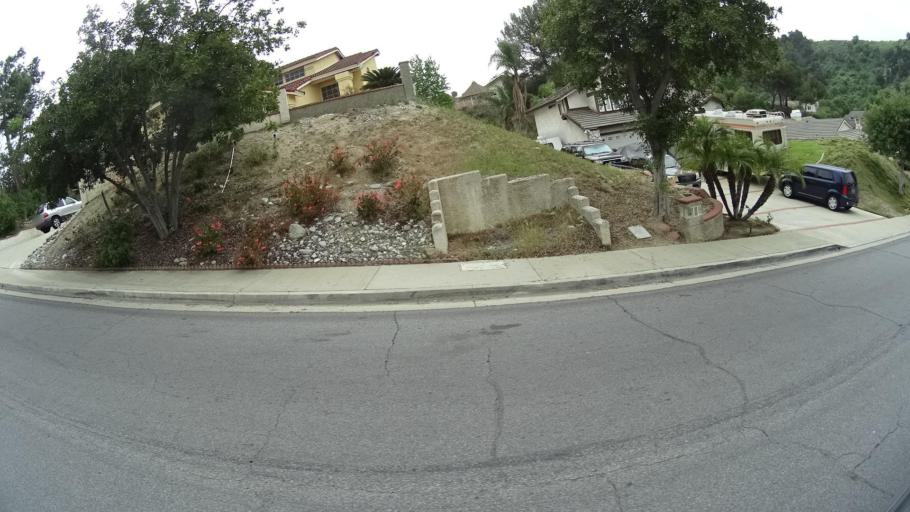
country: US
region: California
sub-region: Los Angeles County
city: Diamond Bar
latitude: 34.0156
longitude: -117.8046
